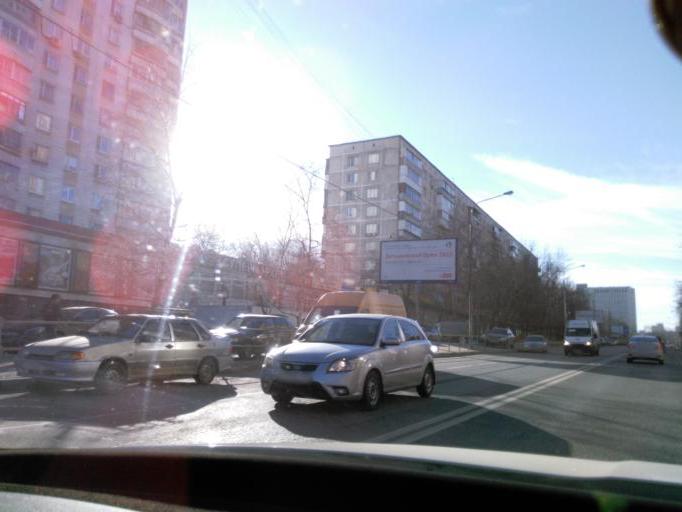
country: RU
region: Moscow
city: Zapadnoye Degunino
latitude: 55.8517
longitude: 37.5193
